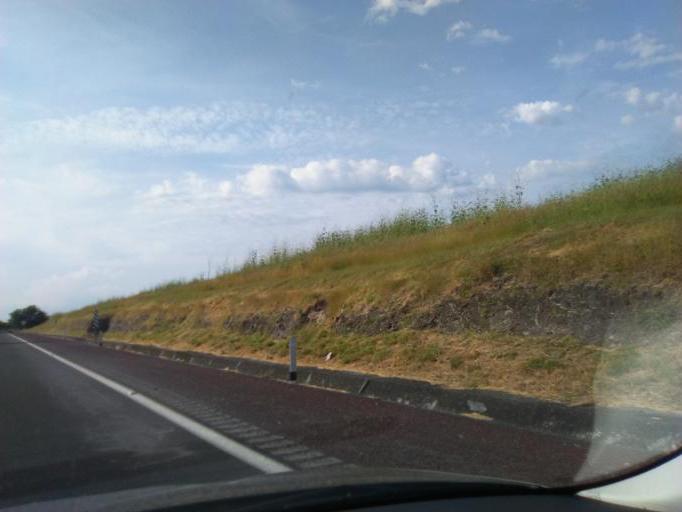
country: MX
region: Morelos
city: Puente de Ixtla
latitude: 18.6005
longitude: -99.2807
